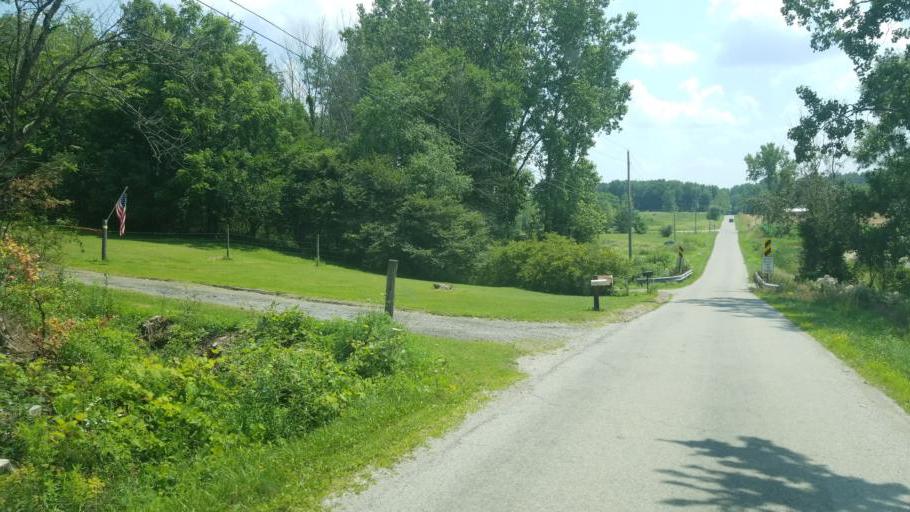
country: US
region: Ohio
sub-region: Richland County
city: Lexington
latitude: 40.6547
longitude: -82.6899
